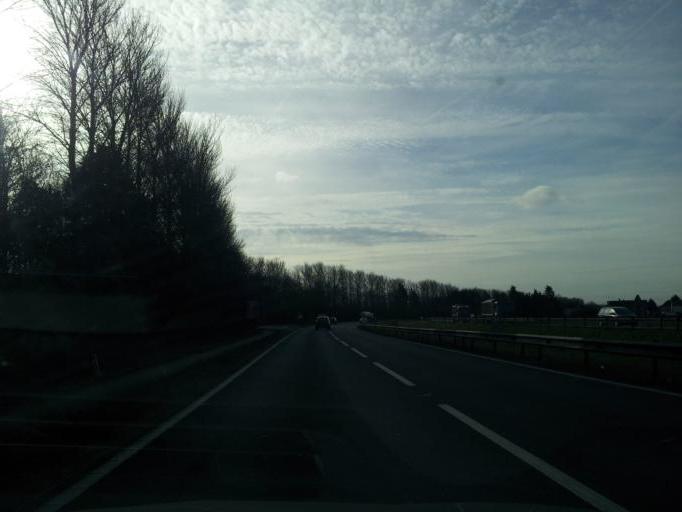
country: GB
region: England
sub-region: Cambridgeshire
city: Little Paxton
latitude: 52.2669
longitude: -0.2618
